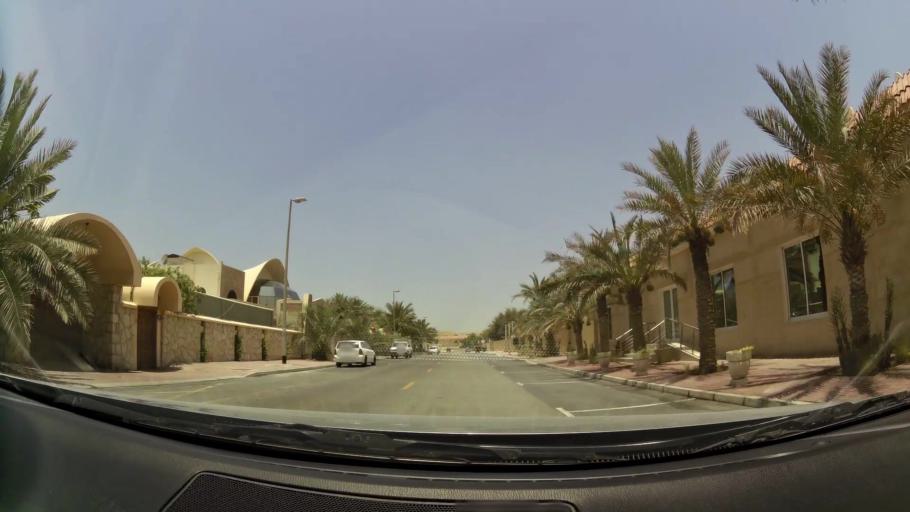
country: AE
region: Dubai
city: Dubai
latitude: 25.1922
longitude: 55.2375
